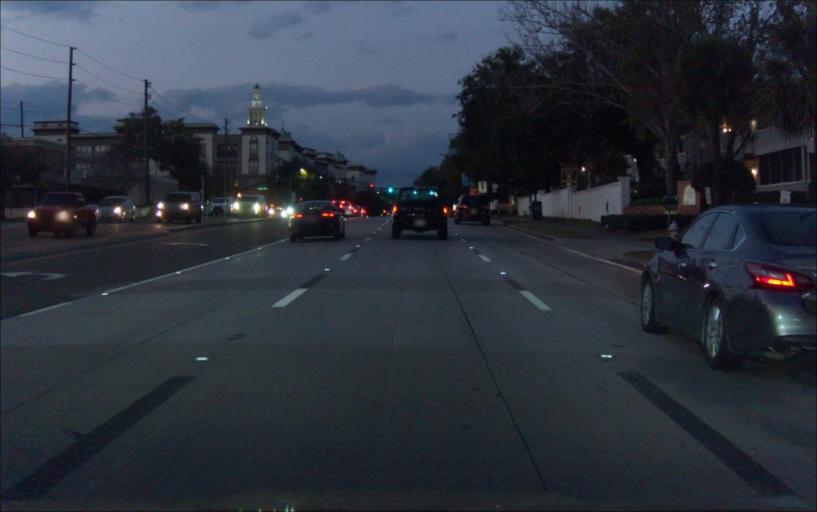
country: US
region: Florida
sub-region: Orange County
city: Maitland
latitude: 28.6206
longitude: -81.3641
